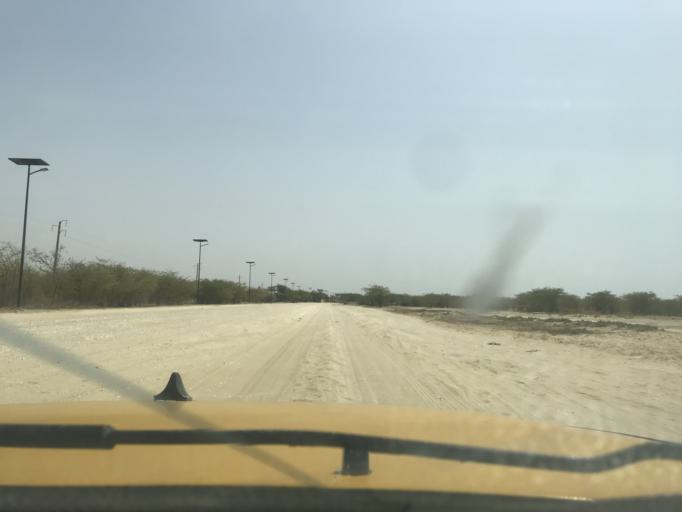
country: SN
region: Saint-Louis
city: Saint-Louis
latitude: 16.0243
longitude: -16.4461
